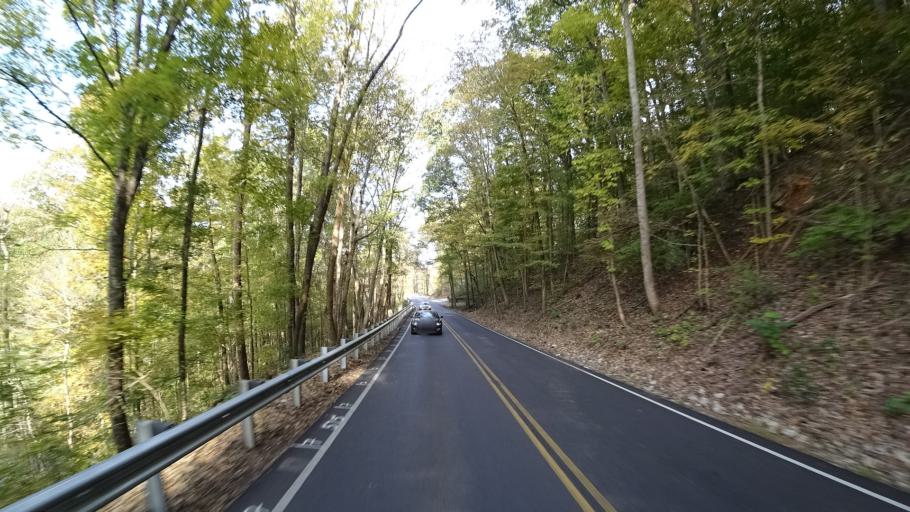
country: US
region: Tennessee
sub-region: Knox County
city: Farragut
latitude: 35.9075
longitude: -84.1881
